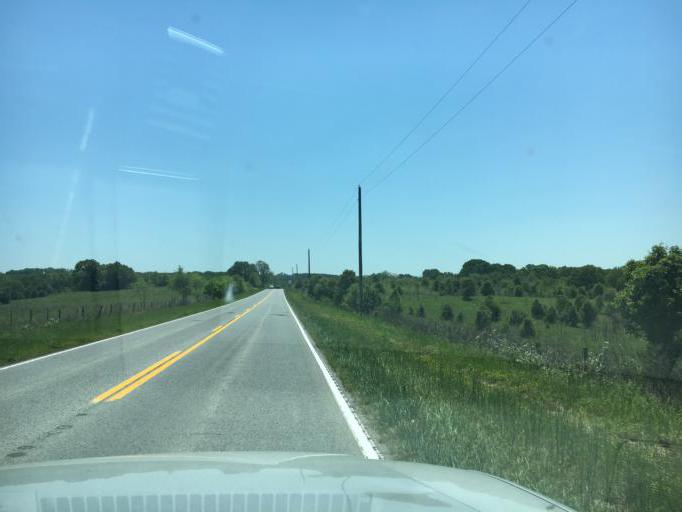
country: US
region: South Carolina
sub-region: Cherokee County
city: Blacksburg
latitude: 35.1664
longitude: -81.5741
